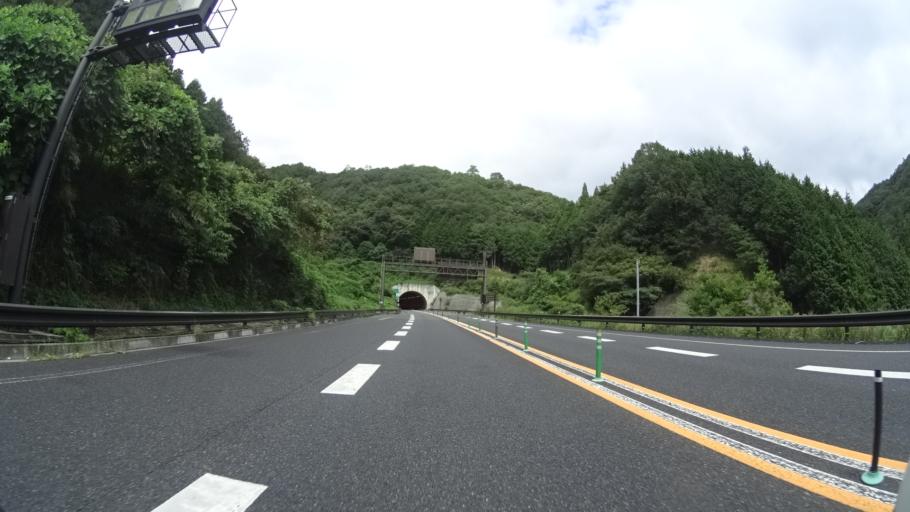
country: JP
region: Hyogo
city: Yamazakicho-nakabirose
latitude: 35.0629
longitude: 134.3627
